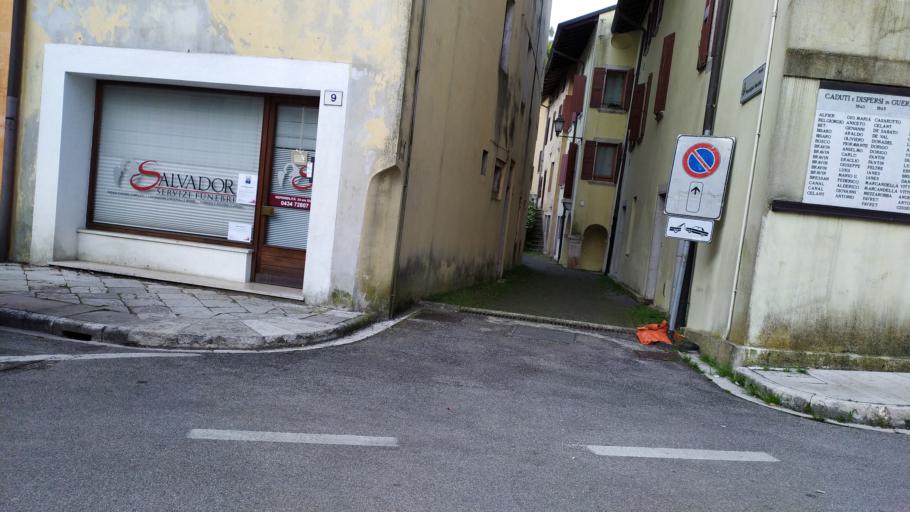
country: IT
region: Friuli Venezia Giulia
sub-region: Provincia di Pordenone
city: Polcenigo
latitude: 46.0307
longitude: 12.5016
